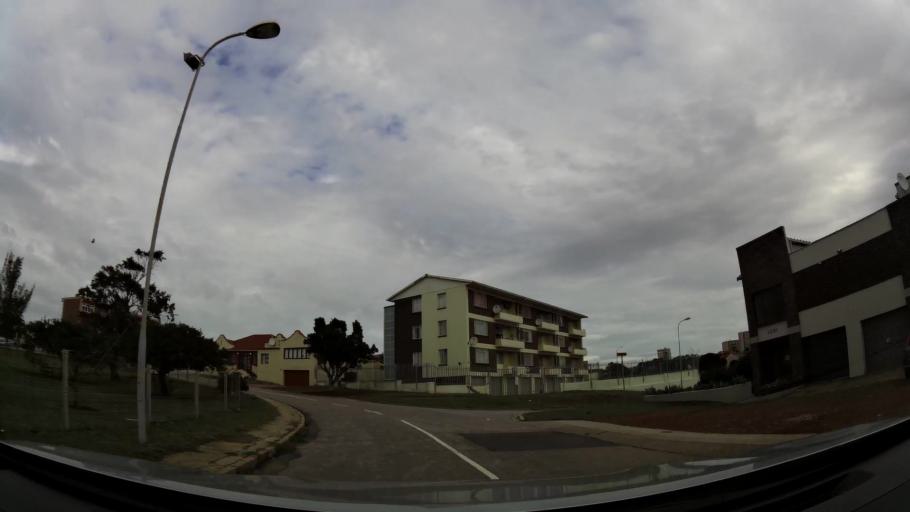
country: ZA
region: Eastern Cape
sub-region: Nelson Mandela Bay Metropolitan Municipality
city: Port Elizabeth
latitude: -33.9574
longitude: 25.6077
